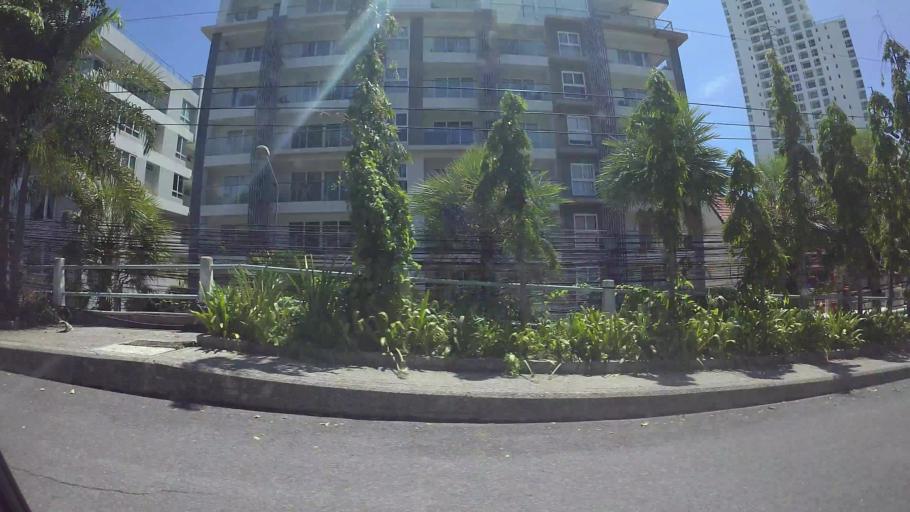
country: TH
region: Chon Buri
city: Phatthaya
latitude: 12.9221
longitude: 100.8642
